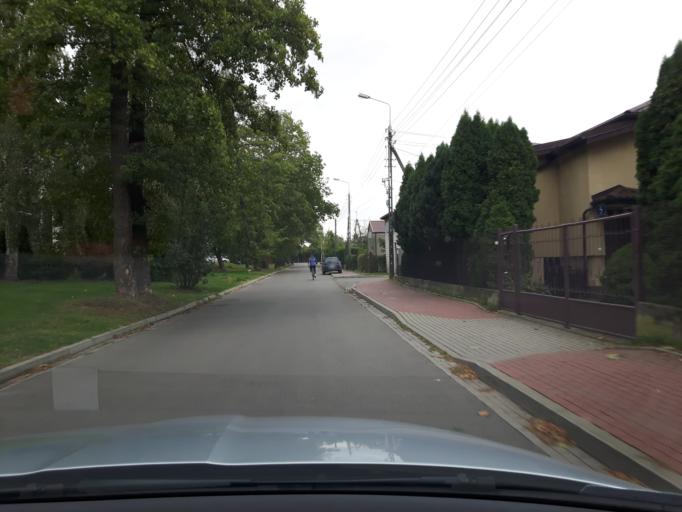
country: PL
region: Masovian Voivodeship
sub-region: Powiat wolominski
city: Kobylka
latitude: 52.3349
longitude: 21.1918
